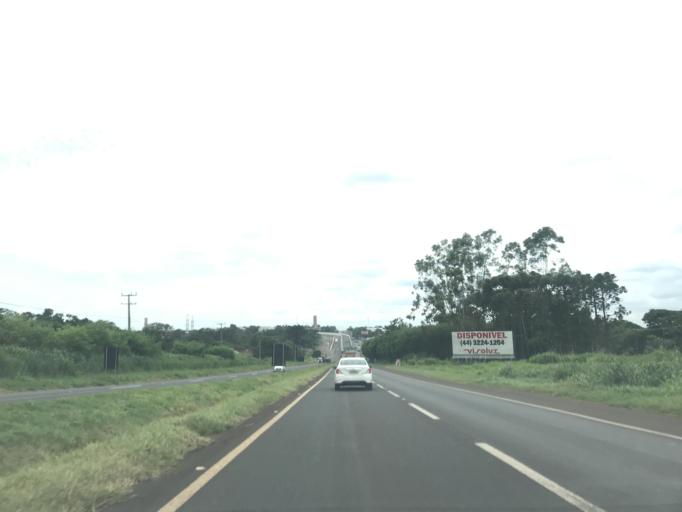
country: BR
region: Parana
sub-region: Maringa
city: Maringa
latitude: -23.4044
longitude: -51.9949
